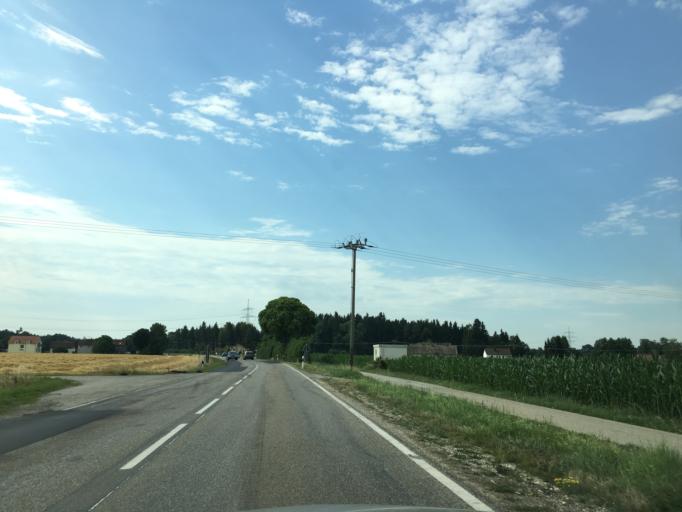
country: DE
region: Bavaria
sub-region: Upper Bavaria
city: Worth
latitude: 48.2378
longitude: 11.9376
